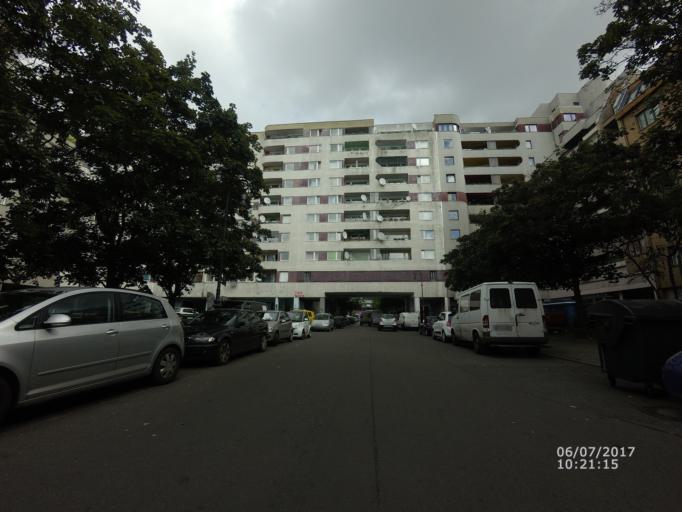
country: DE
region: Berlin
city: Bezirk Kreuzberg
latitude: 52.4978
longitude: 13.4168
